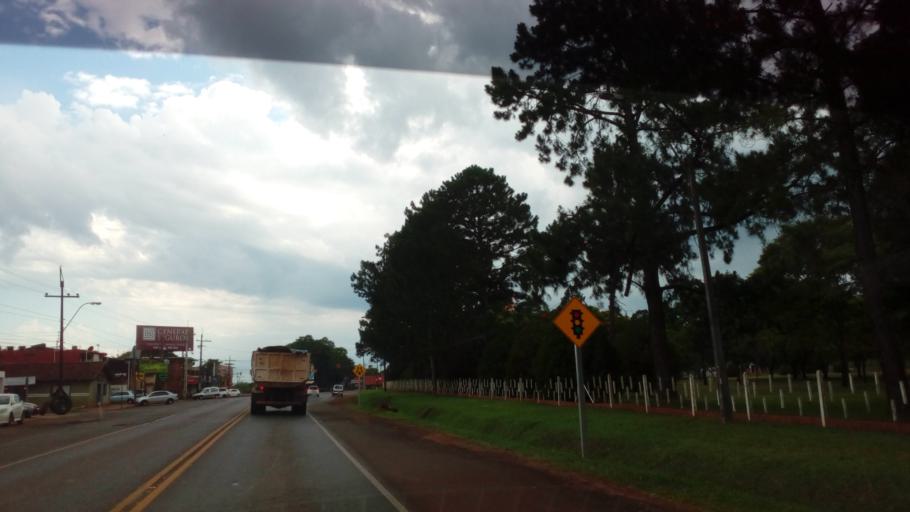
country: PY
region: Itapua
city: Obligado
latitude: -27.0739
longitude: -55.6404
